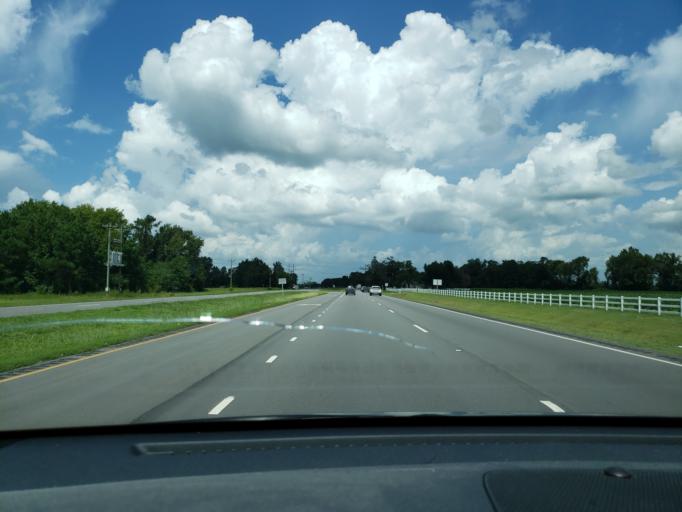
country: US
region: North Carolina
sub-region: Robeson County
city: Saint Pauls
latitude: 34.7701
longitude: -78.8104
